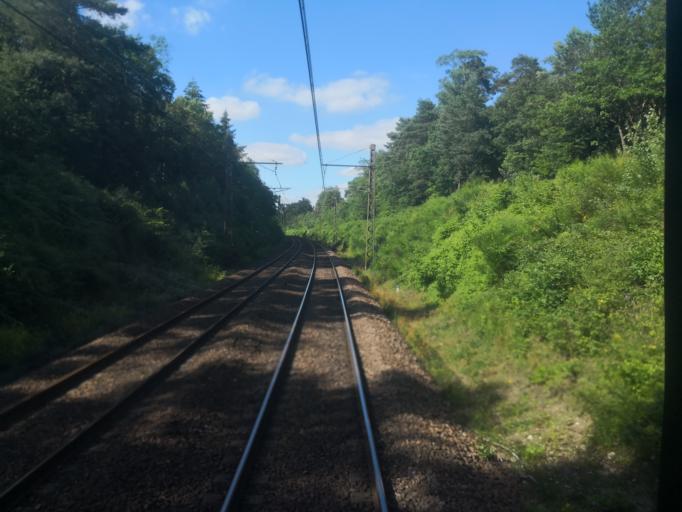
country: FR
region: Ile-de-France
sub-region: Departement de Seine-et-Marne
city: Samoreau
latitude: 48.4289
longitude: 2.7372
